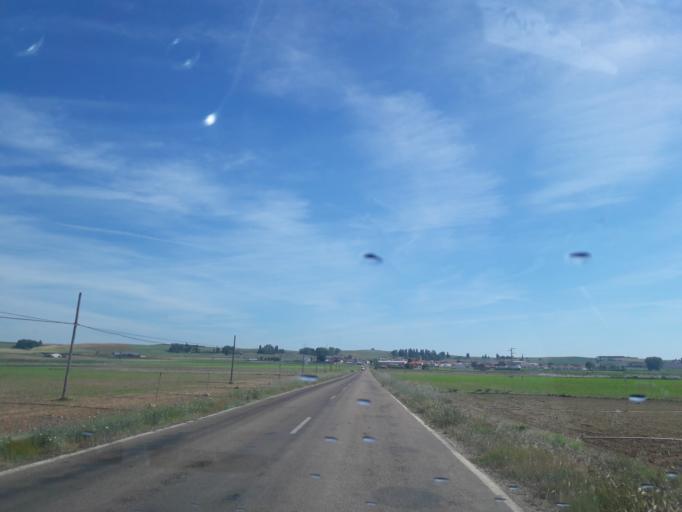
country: ES
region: Castille and Leon
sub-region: Provincia de Salamanca
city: Villoruela
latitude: 40.9954
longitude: -5.4023
